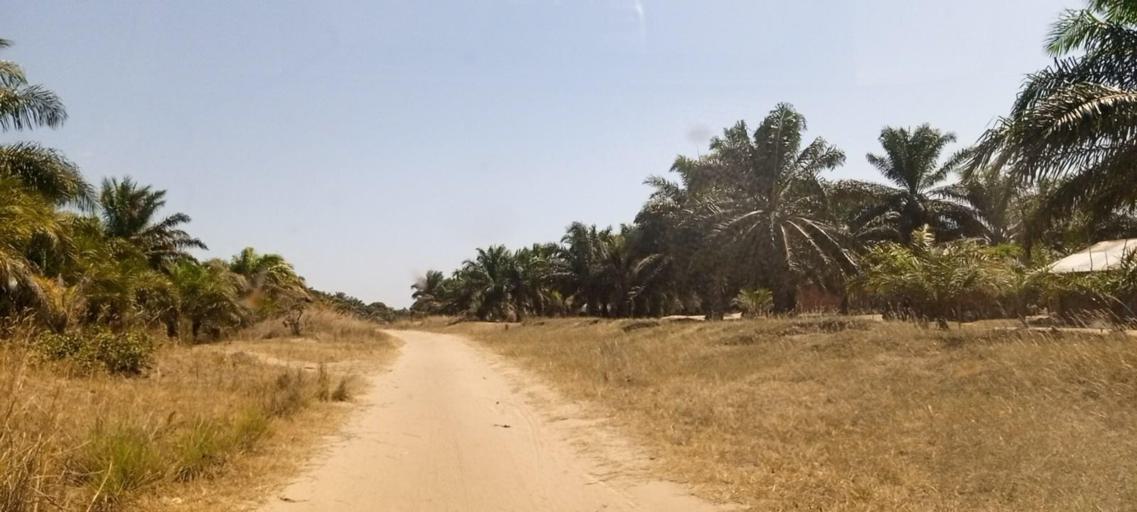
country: CD
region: Kasai-Oriental
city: Kabinda
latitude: -5.9643
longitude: 24.7661
